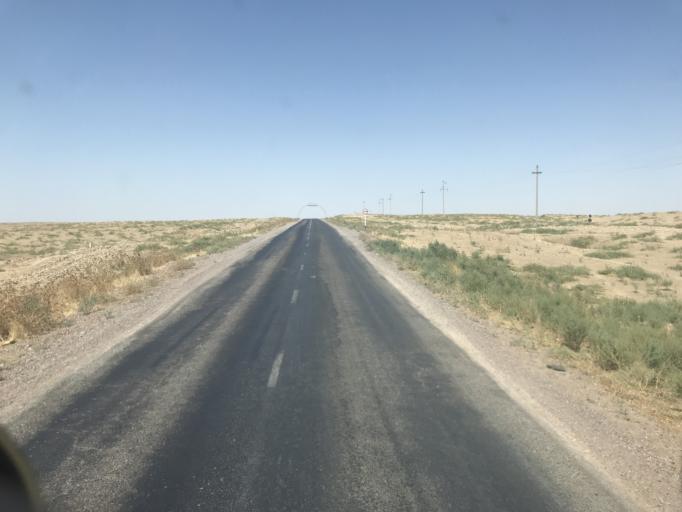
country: UZ
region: Toshkent
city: Chinoz
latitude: 41.1359
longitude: 68.7140
